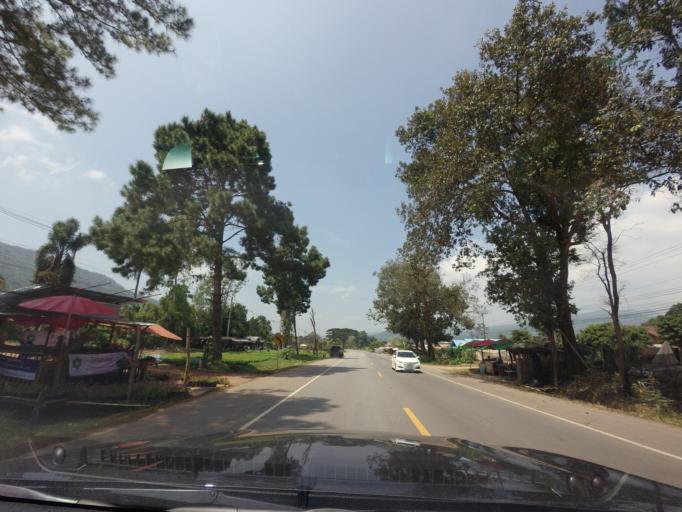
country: TH
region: Loei
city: Phu Ruea
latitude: 17.4593
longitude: 101.4039
